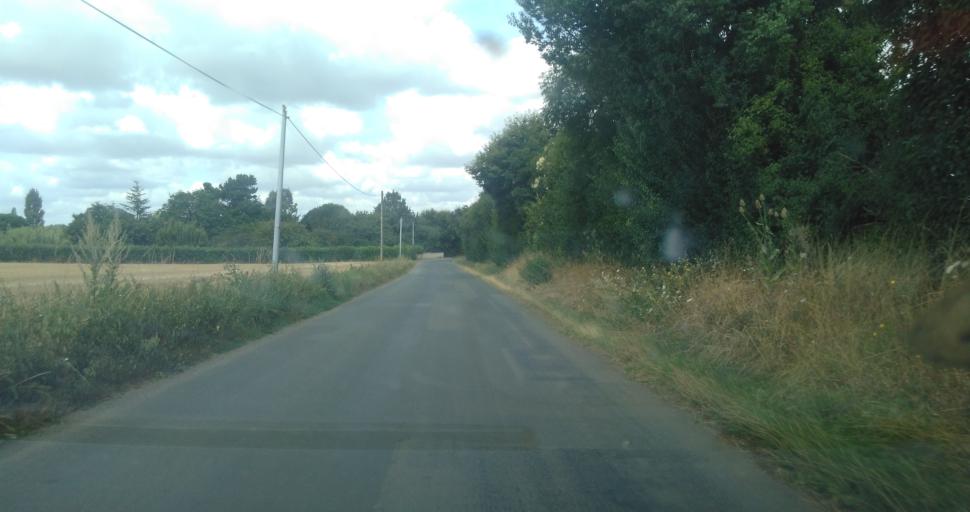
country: FR
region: Pays de la Loire
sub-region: Departement de la Vendee
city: Sainte-Hermine
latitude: 46.5322
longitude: -1.0834
